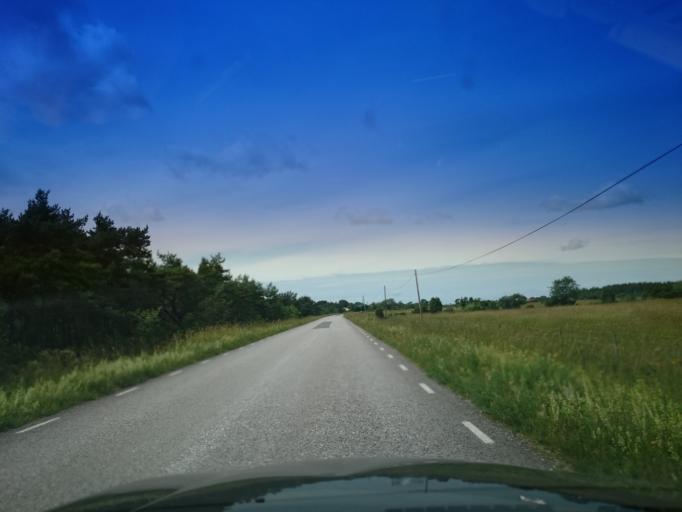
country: SE
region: Gotland
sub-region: Gotland
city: Hemse
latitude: 57.2497
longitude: 18.5628
